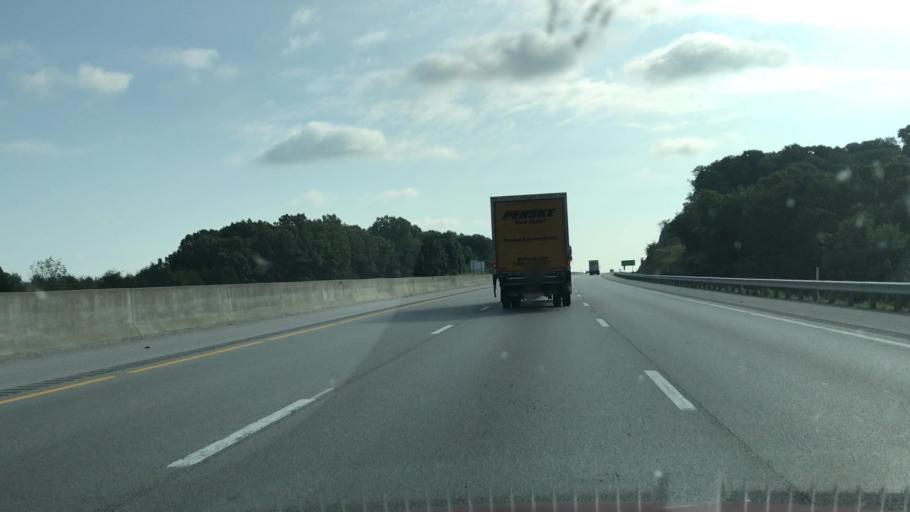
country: US
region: Kentucky
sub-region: Barren County
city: Cave City
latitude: 37.1034
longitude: -86.0468
